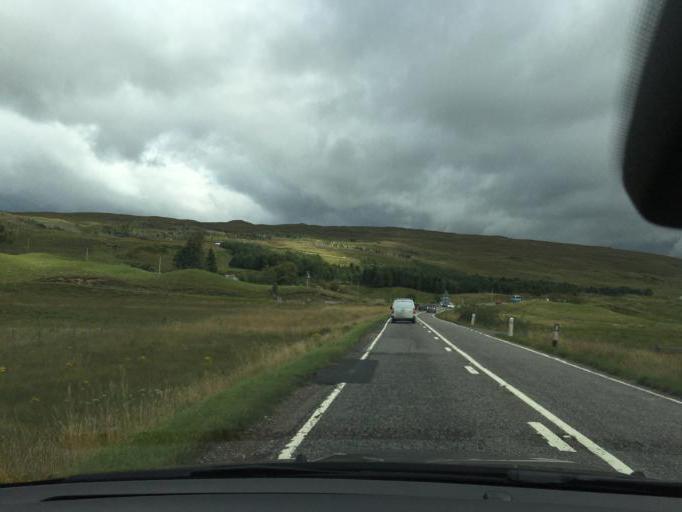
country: GB
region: Scotland
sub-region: Highland
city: Spean Bridge
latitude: 56.5615
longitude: -4.7459
